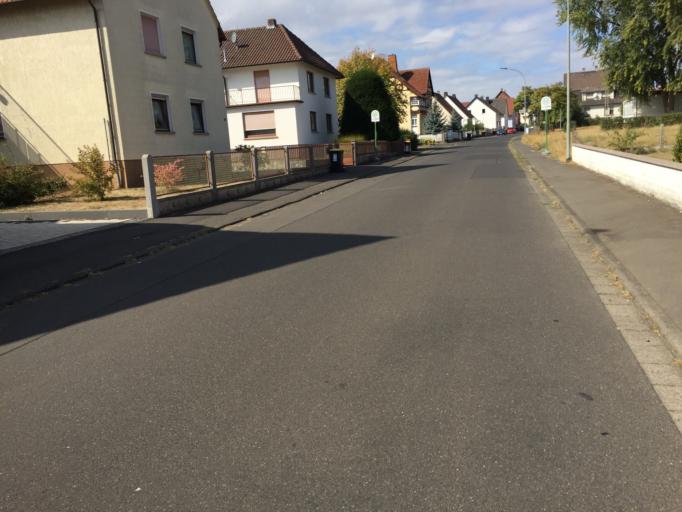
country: DE
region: Hesse
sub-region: Regierungsbezirk Darmstadt
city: Wolfersheim
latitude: 50.4482
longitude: 8.8432
